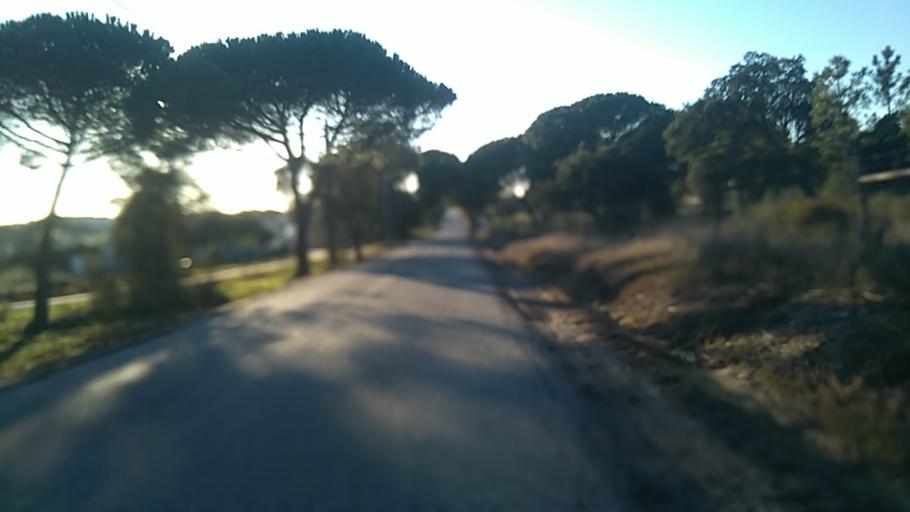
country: PT
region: Evora
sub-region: Vendas Novas
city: Vendas Novas
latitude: 38.8067
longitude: -8.4073
